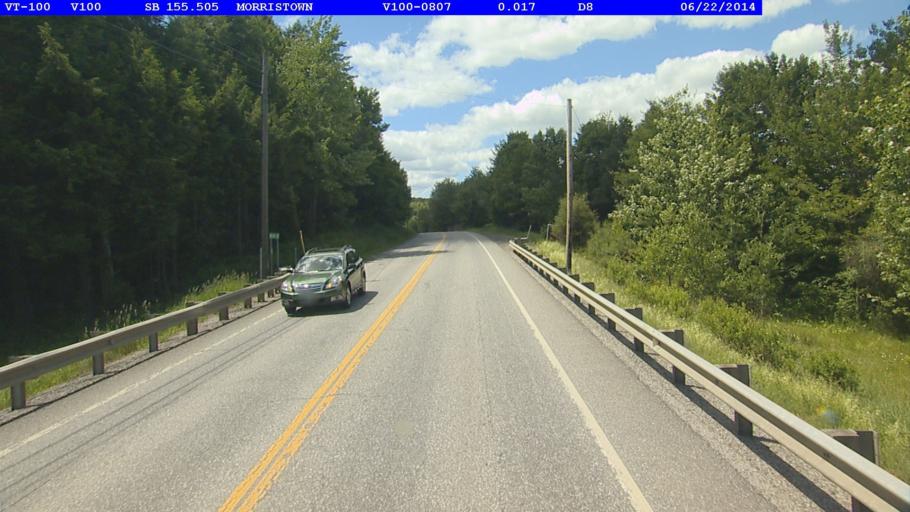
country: US
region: Vermont
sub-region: Lamoille County
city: Morristown
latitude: 44.4951
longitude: -72.6354
